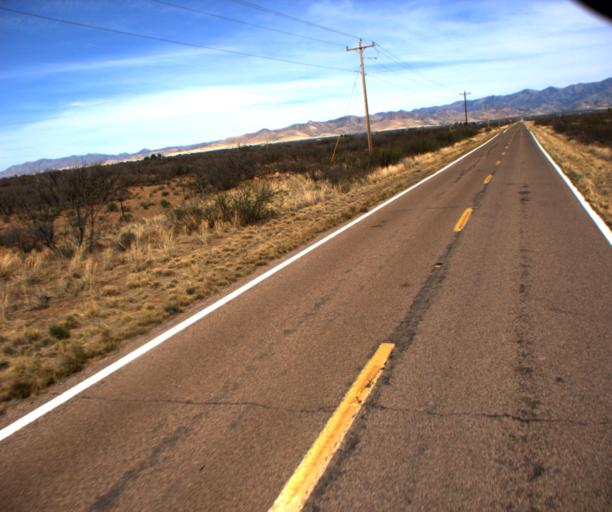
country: US
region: Arizona
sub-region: Cochise County
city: Willcox
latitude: 31.8760
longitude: -109.5641
